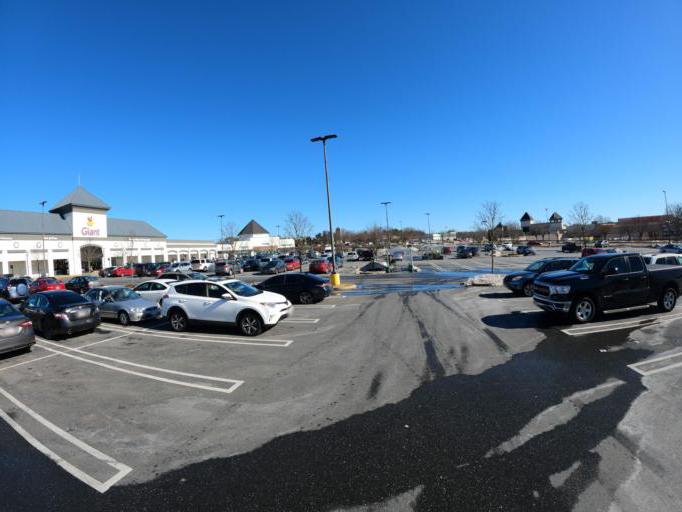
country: US
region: Maryland
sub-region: Montgomery County
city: Germantown
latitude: 39.2031
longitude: -77.2481
